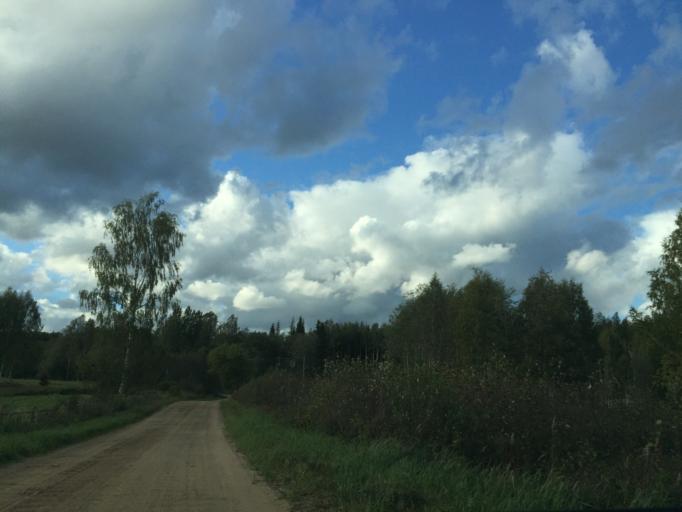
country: LV
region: Ligatne
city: Ligatne
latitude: 57.1337
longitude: 25.0996
